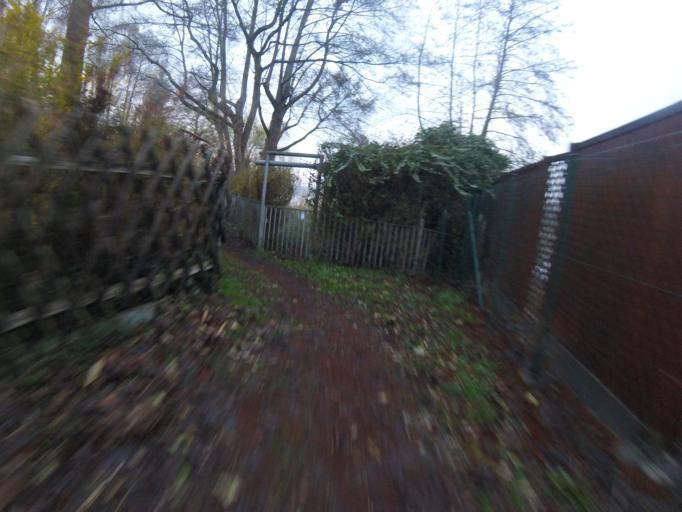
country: DE
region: Brandenburg
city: Konigs Wusterhausen
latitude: 52.2895
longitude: 13.6777
